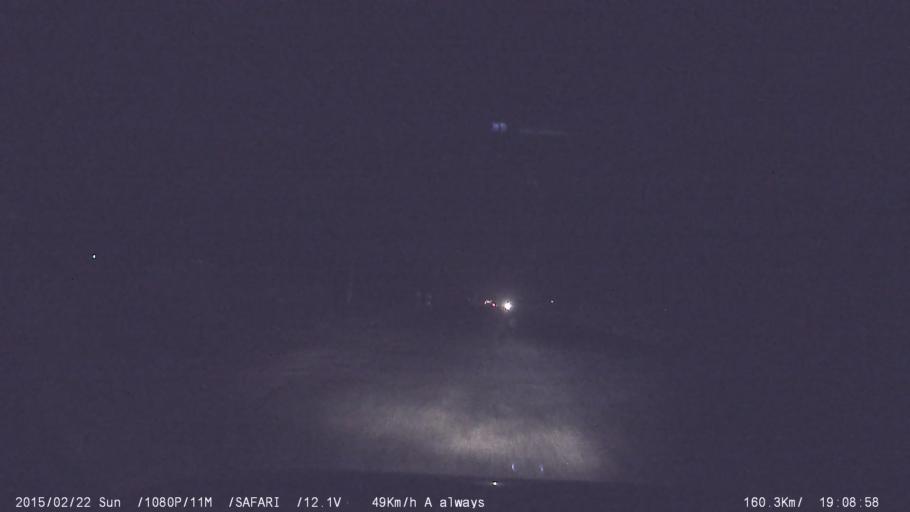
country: IN
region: Tamil Nadu
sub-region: Theni
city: Teni
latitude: 10.0536
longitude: 77.5049
